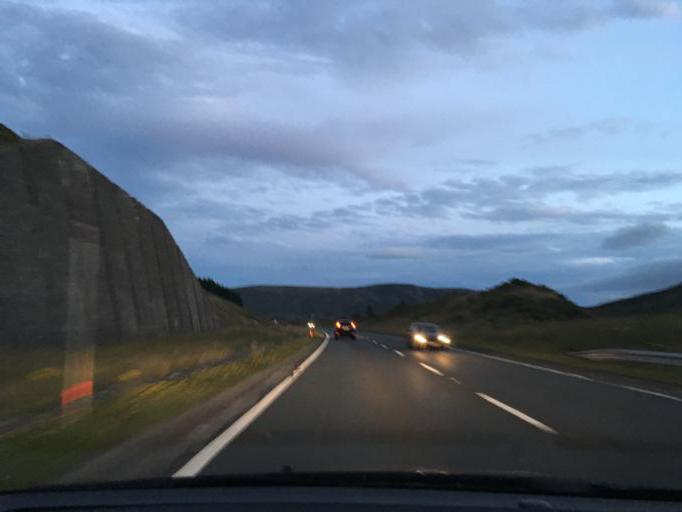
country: GB
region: Scotland
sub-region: Highland
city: Kingussie
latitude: 56.8468
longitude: -4.2407
